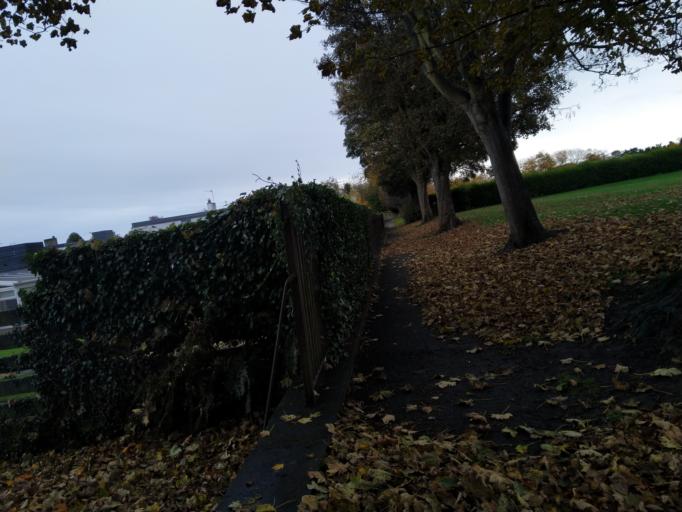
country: GB
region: Scotland
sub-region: East Lothian
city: Tranent
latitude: 55.9455
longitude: -2.9676
